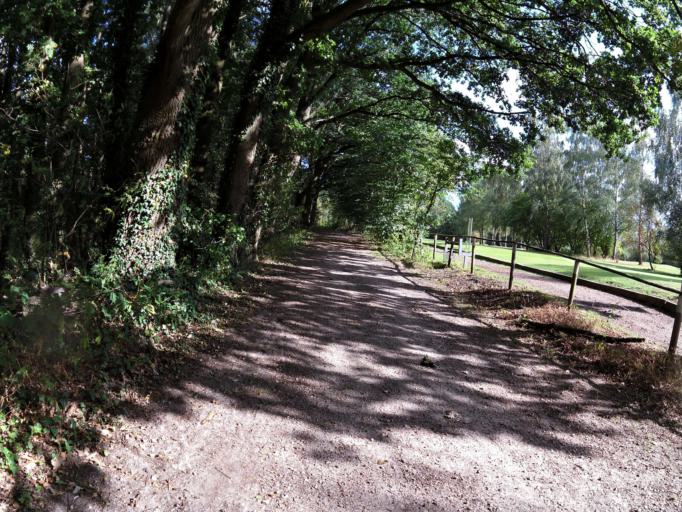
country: DE
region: Lower Saxony
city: Hamersen
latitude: 53.2751
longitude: 9.4804
